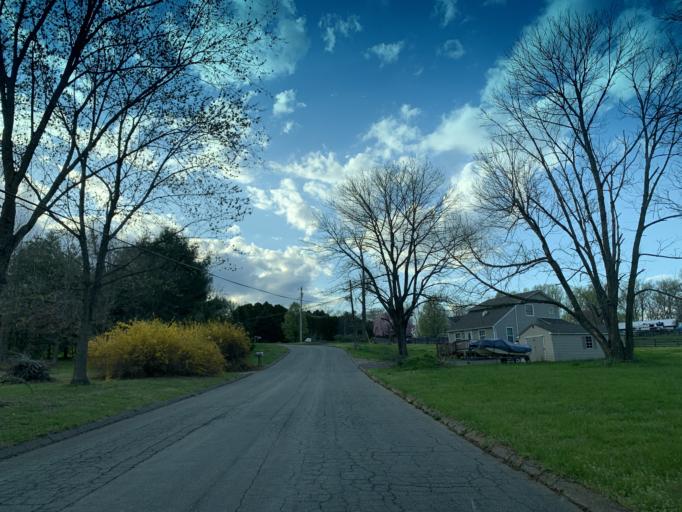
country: US
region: Maryland
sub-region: Harford County
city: South Bel Air
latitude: 39.6108
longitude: -76.2838
